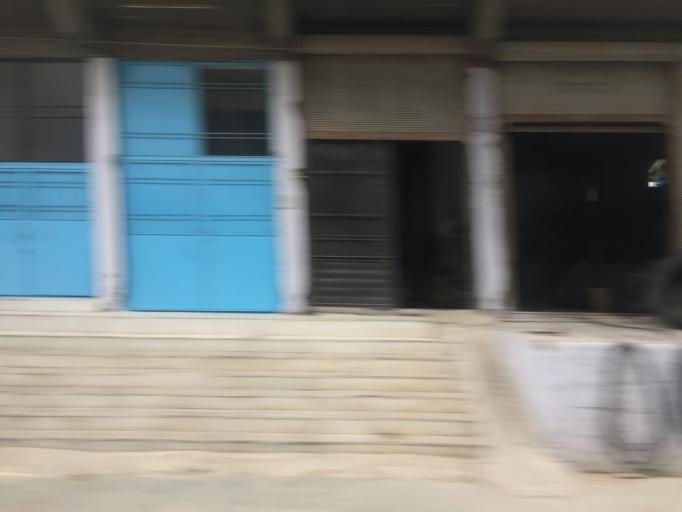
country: TR
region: Gaziantep
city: Gaziantep
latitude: 37.0709
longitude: 37.4134
